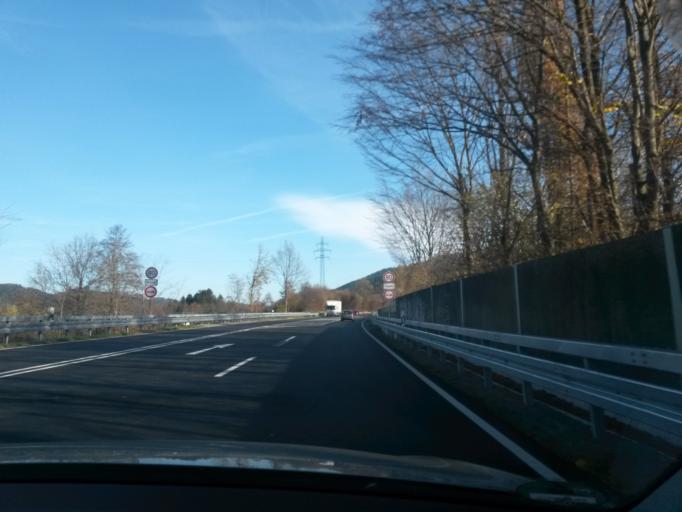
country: DE
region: Baden-Wuerttemberg
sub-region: Freiburg Region
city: Gutach im Breisgau
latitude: 48.1091
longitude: 7.9866
